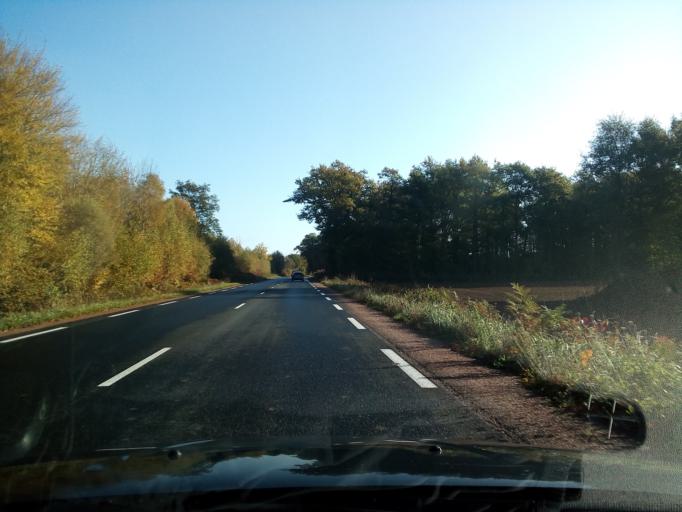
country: FR
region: Limousin
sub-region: Departement de la Haute-Vienne
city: Magnac-Laval
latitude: 46.1845
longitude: 1.1993
